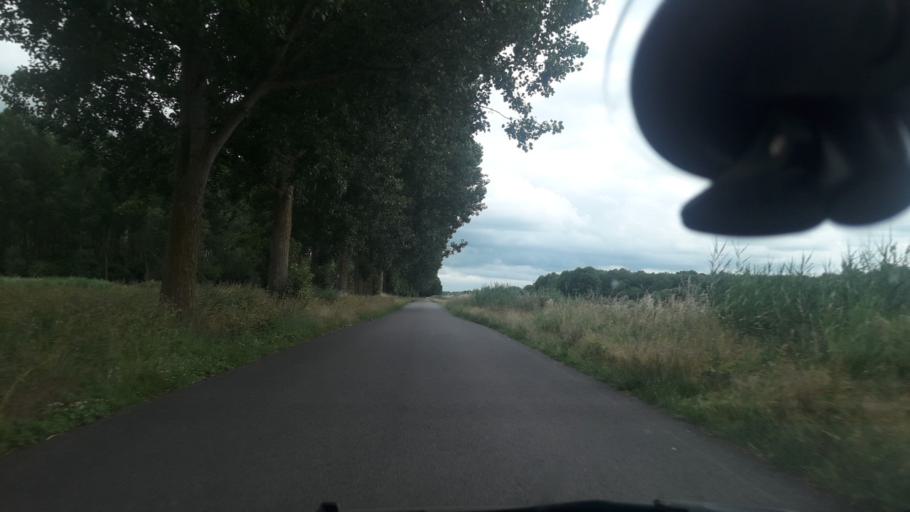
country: NL
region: North Holland
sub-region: Gemeente Huizen
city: Huizen
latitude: 52.3530
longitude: 5.2768
